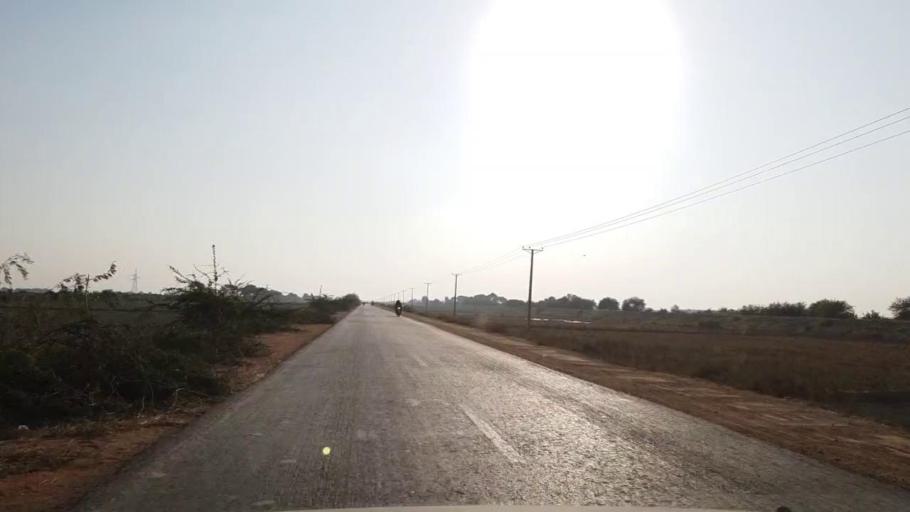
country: PK
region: Sindh
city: Mirpur Batoro
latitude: 24.7682
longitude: 68.2791
